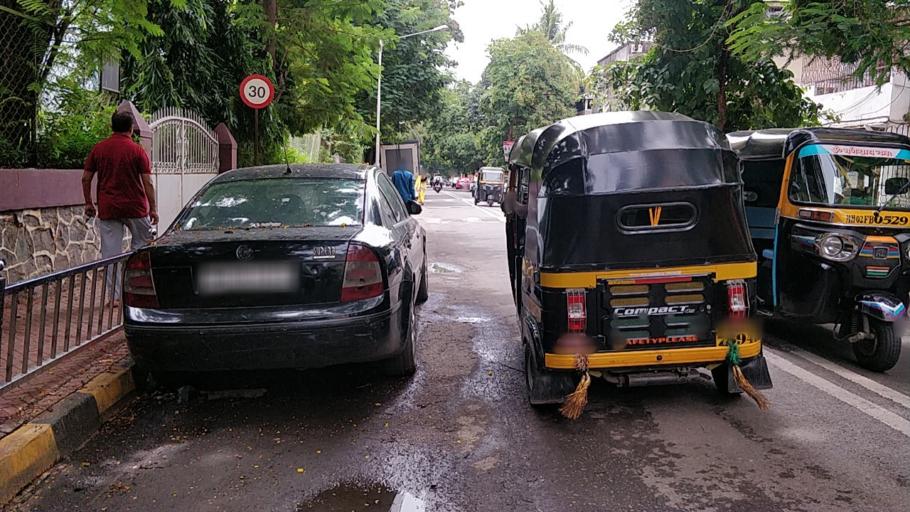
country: IN
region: Maharashtra
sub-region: Mumbai Suburban
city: Mumbai
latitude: 19.0623
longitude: 72.8330
